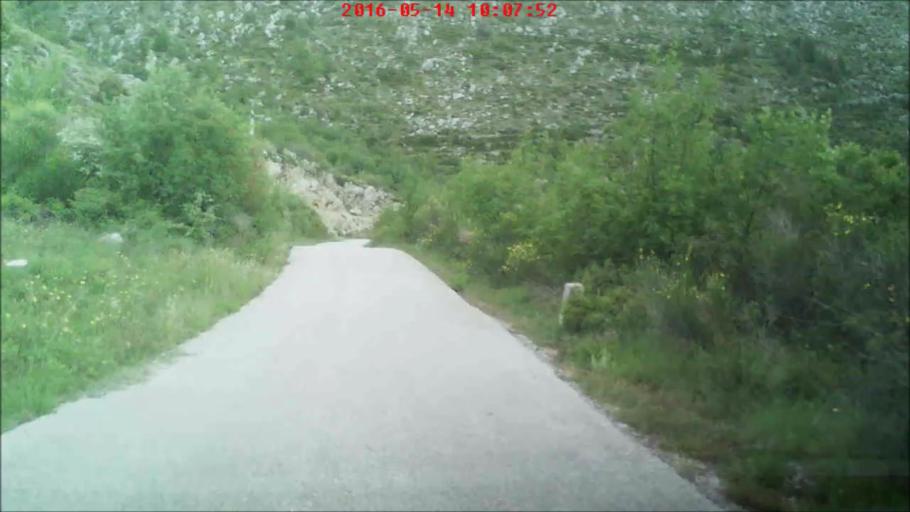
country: HR
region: Dubrovacko-Neretvanska
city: Podgora
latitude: 42.7489
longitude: 17.9323
